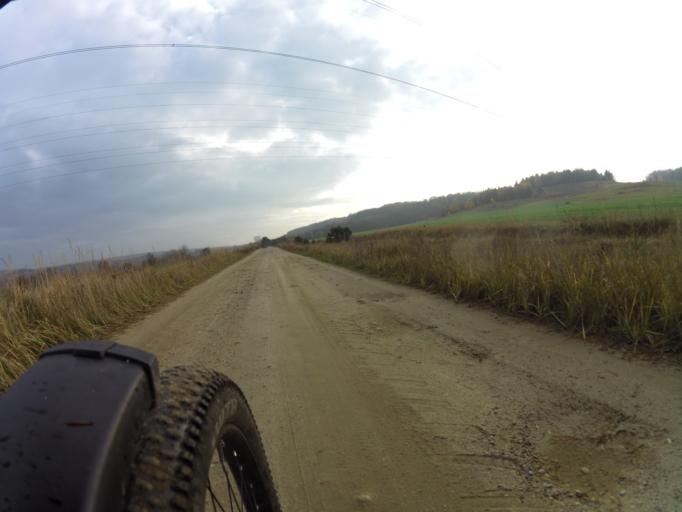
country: PL
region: Pomeranian Voivodeship
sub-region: Powiat wejherowski
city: Gniewino
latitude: 54.7083
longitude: 18.1003
